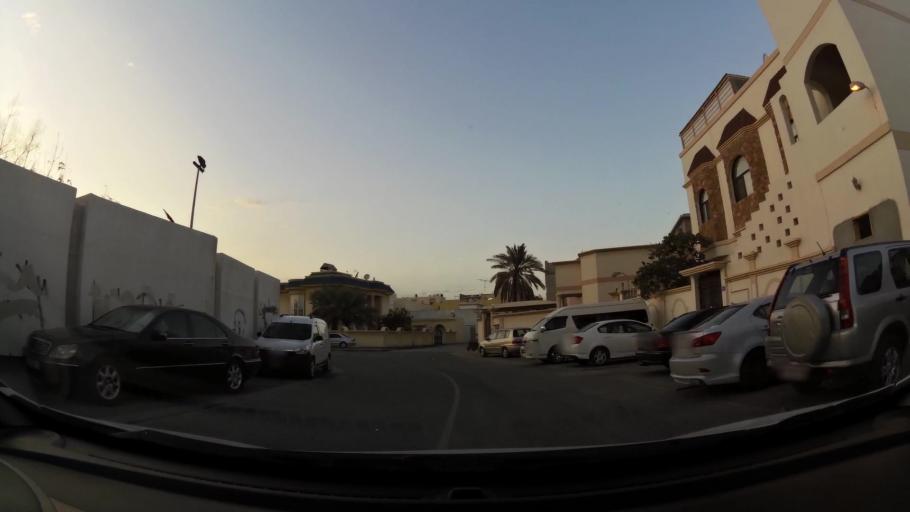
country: BH
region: Manama
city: Jidd Hafs
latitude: 26.2267
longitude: 50.5356
